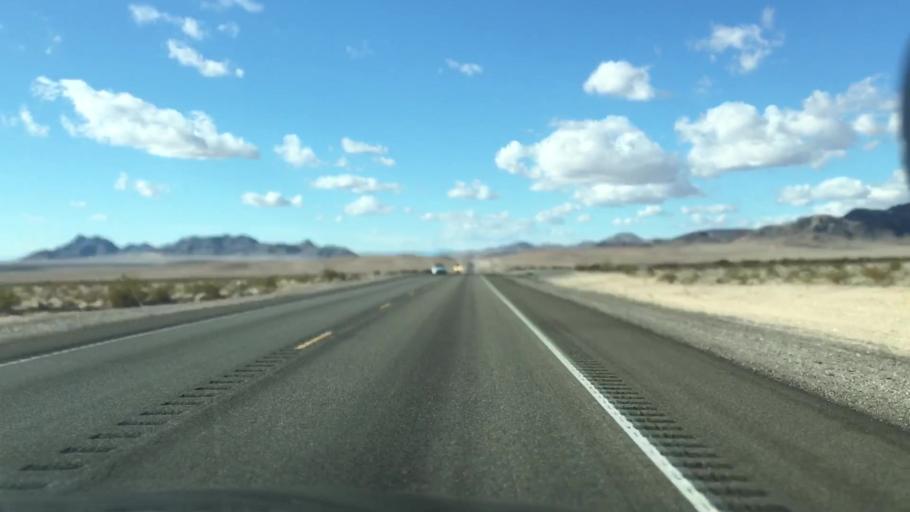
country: US
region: Nevada
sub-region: Nye County
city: Pahrump
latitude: 36.6027
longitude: -116.2518
